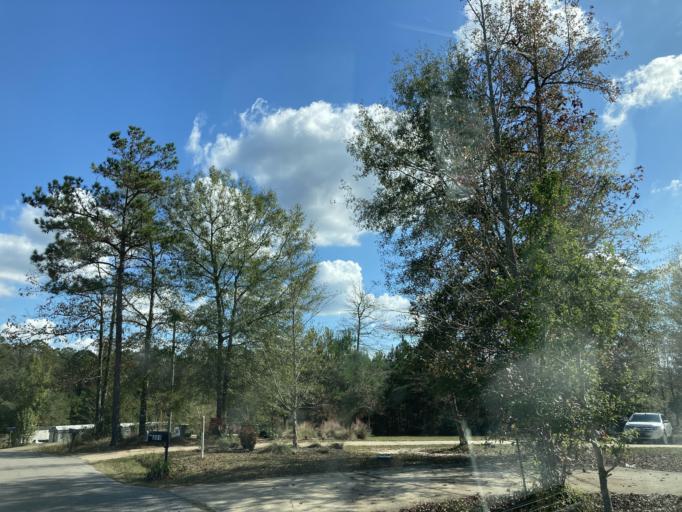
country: US
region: Mississippi
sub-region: Lamar County
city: Sumrall
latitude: 31.3610
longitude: -89.5499
